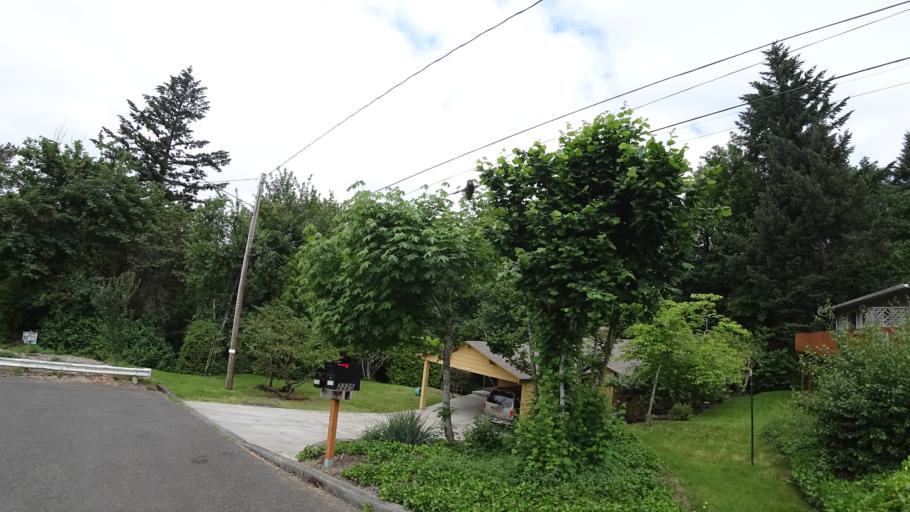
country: US
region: Oregon
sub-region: Multnomah County
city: Portland
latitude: 45.4805
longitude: -122.6999
